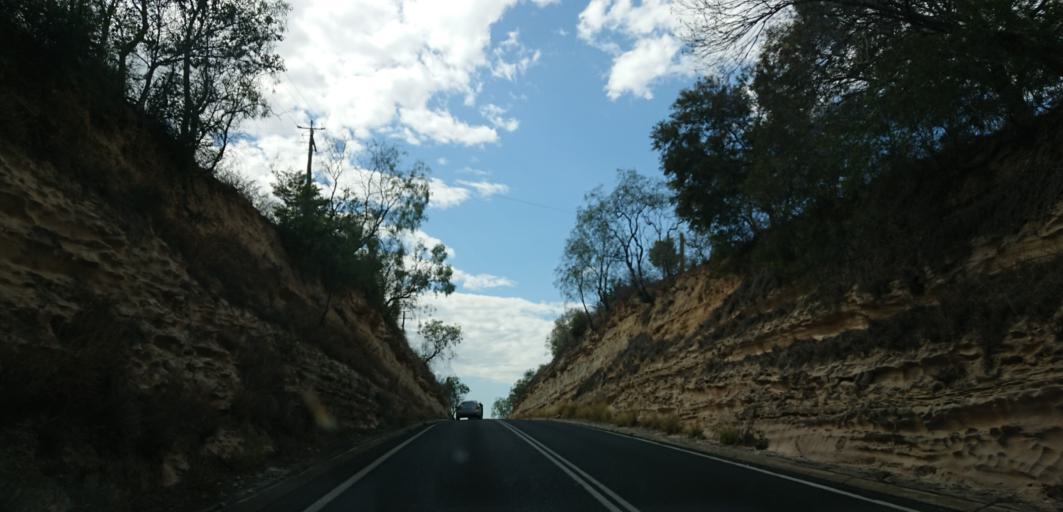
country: AU
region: Queensland
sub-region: Lockyer Valley
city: Gatton
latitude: -27.6596
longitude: 152.1644
